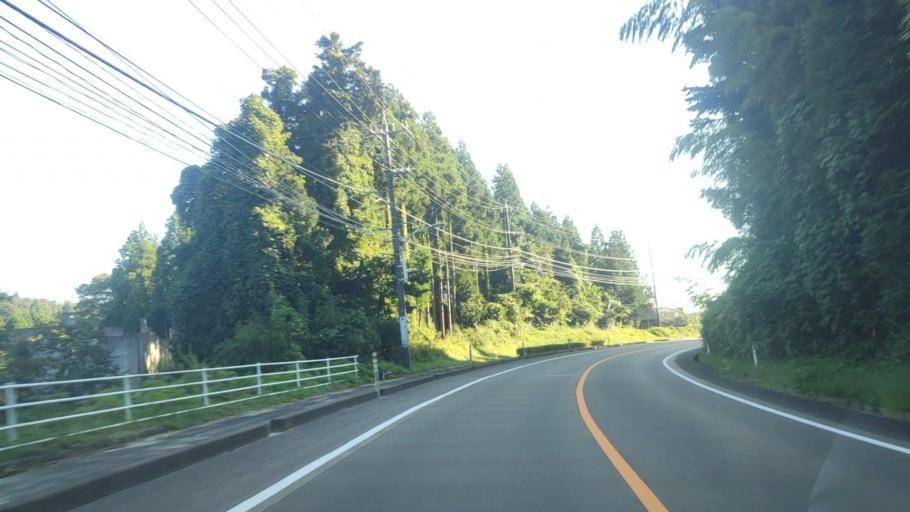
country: JP
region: Ishikawa
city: Nanao
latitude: 37.1187
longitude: 136.8617
